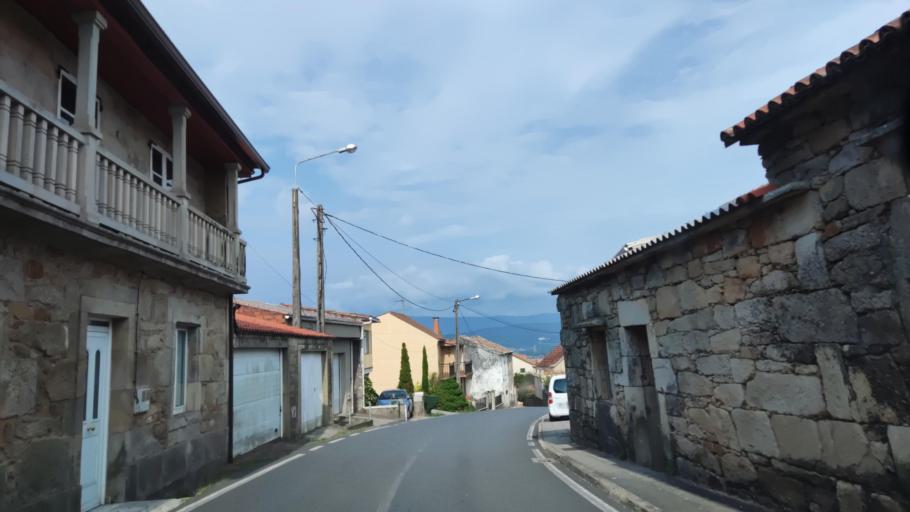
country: ES
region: Galicia
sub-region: Provincia da Coruna
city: Rianxo
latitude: 42.6477
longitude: -8.8103
